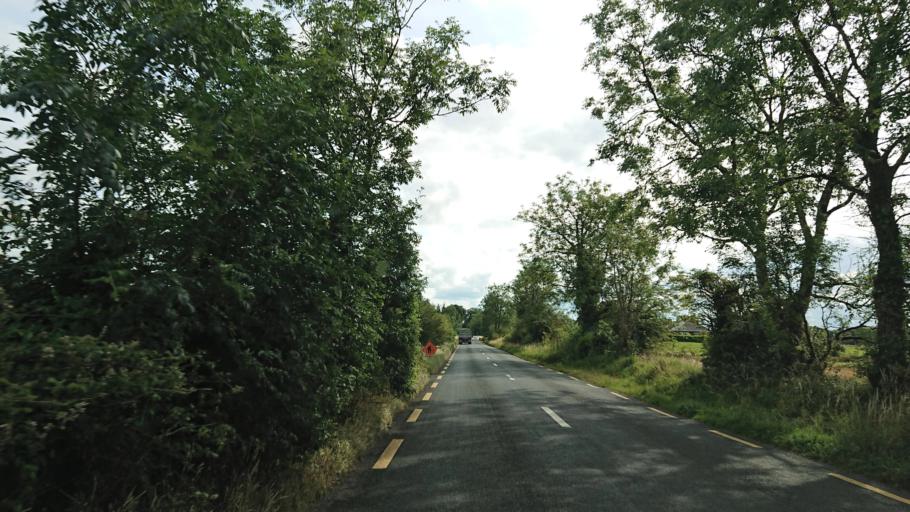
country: IE
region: Connaught
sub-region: County Leitrim
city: Carrick-on-Shannon
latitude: 53.9699
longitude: -8.0663
